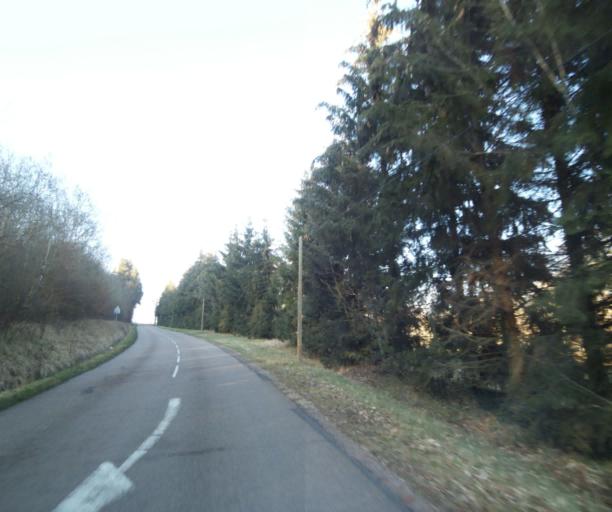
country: FR
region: Champagne-Ardenne
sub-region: Departement de la Haute-Marne
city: Bienville
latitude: 48.5566
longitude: 5.0867
